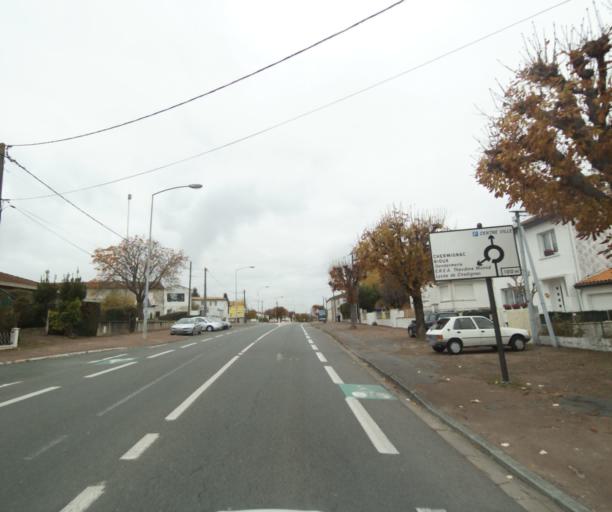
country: FR
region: Poitou-Charentes
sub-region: Departement de la Charente-Maritime
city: Saintes
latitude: 45.7329
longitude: -0.6456
